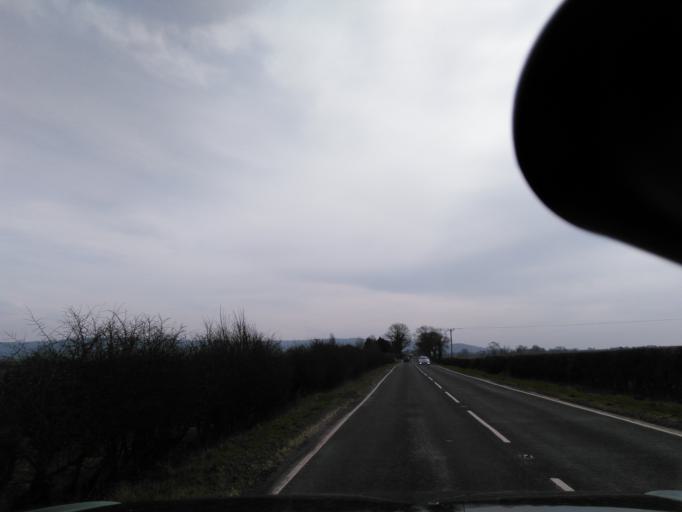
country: GB
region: England
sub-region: North Yorkshire
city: Thirsk
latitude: 54.2329
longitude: -1.3037
